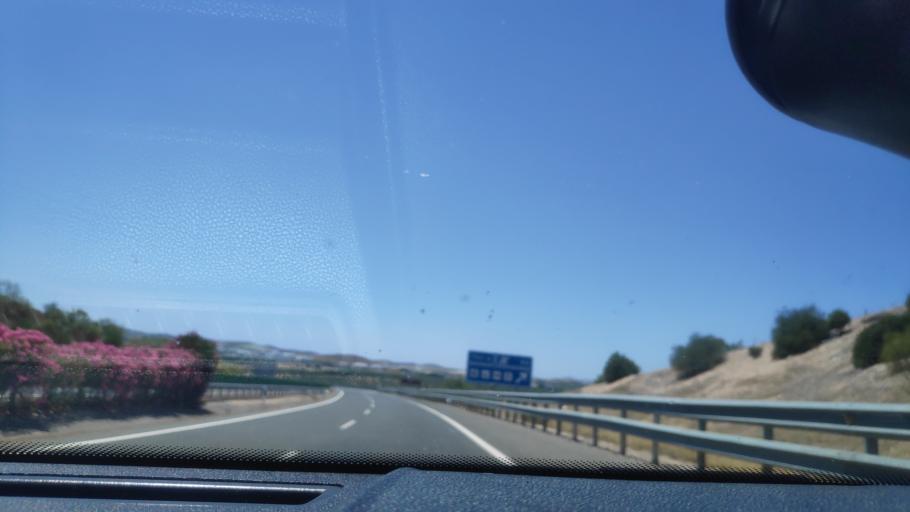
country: ES
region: Andalusia
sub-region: Provincia de Jaen
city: Jaen
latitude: 37.8216
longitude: -3.7492
